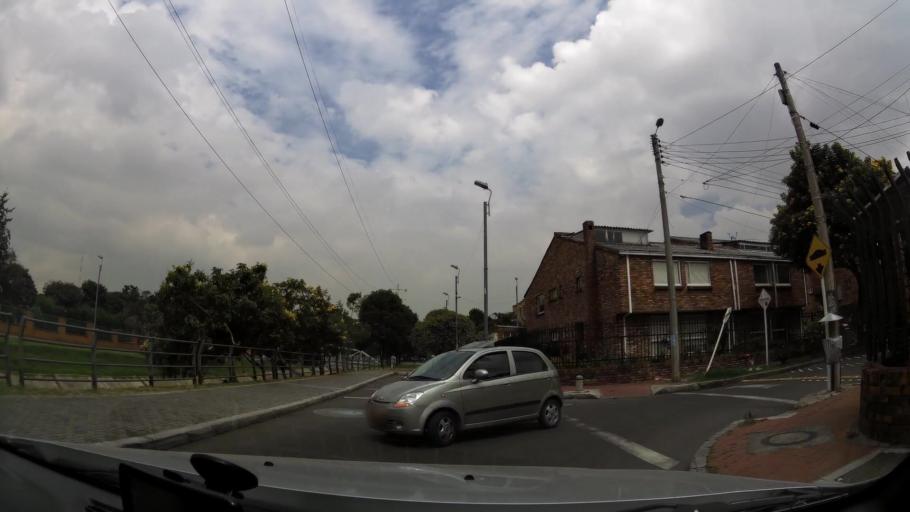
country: CO
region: Bogota D.C.
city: Barrio San Luis
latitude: 4.6829
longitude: -74.0702
